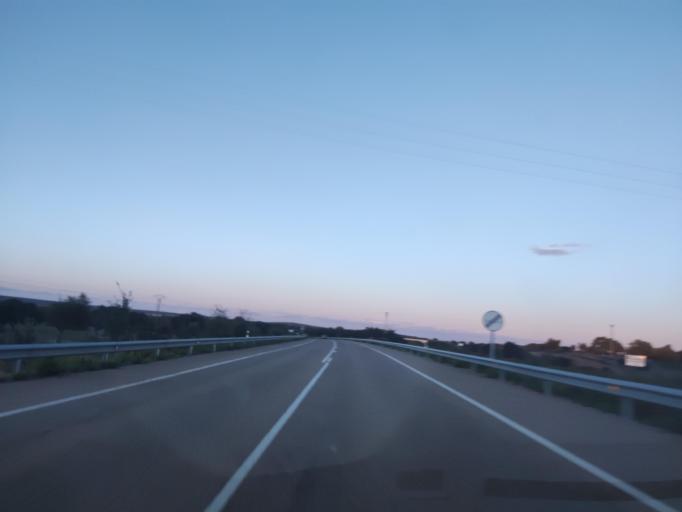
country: ES
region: Castille and Leon
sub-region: Provincia de Salamanca
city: San Munoz
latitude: 40.8175
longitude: -6.1260
